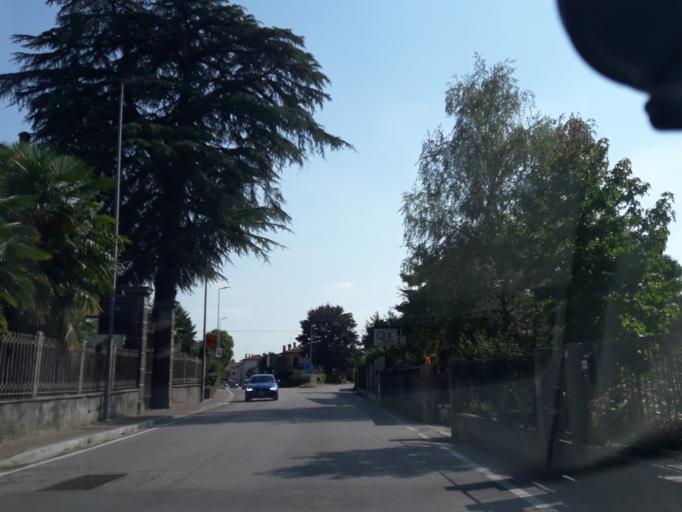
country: IT
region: Friuli Venezia Giulia
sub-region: Provincia di Udine
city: Reana del Roiale
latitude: 46.1270
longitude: 13.2145
